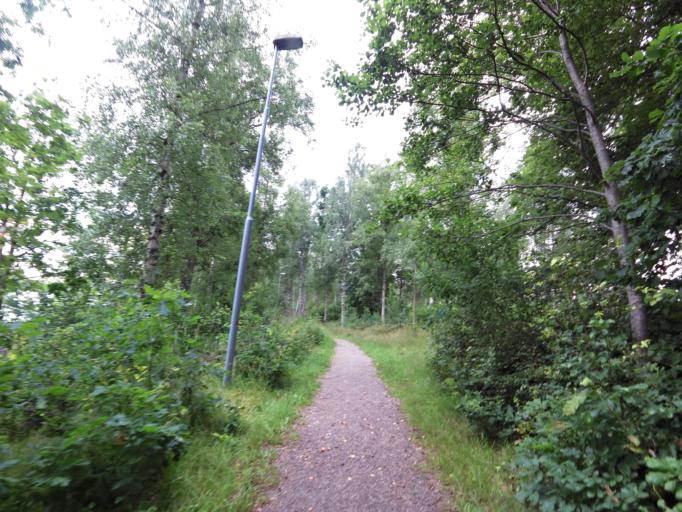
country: SE
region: Blekinge
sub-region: Olofstroms Kommun
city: Olofstroem
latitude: 56.3500
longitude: 14.5925
